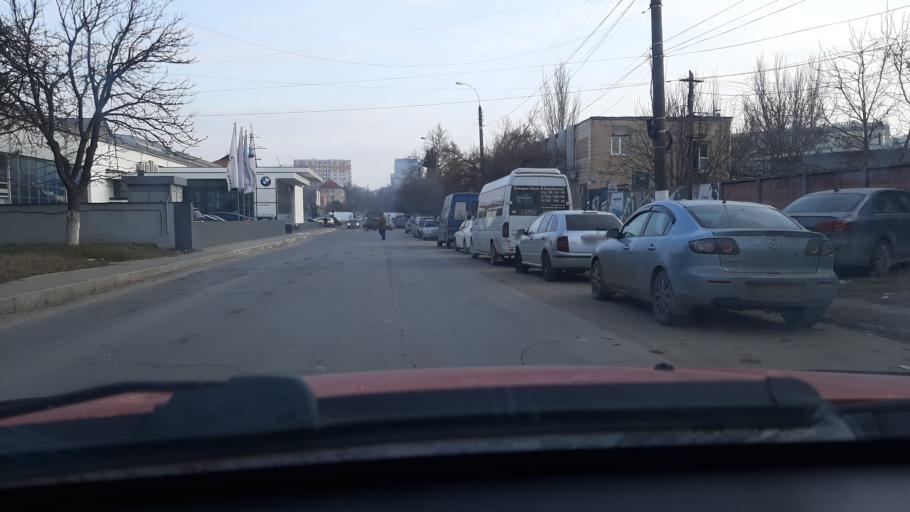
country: MD
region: Chisinau
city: Chisinau
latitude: 47.0416
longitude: 28.8112
